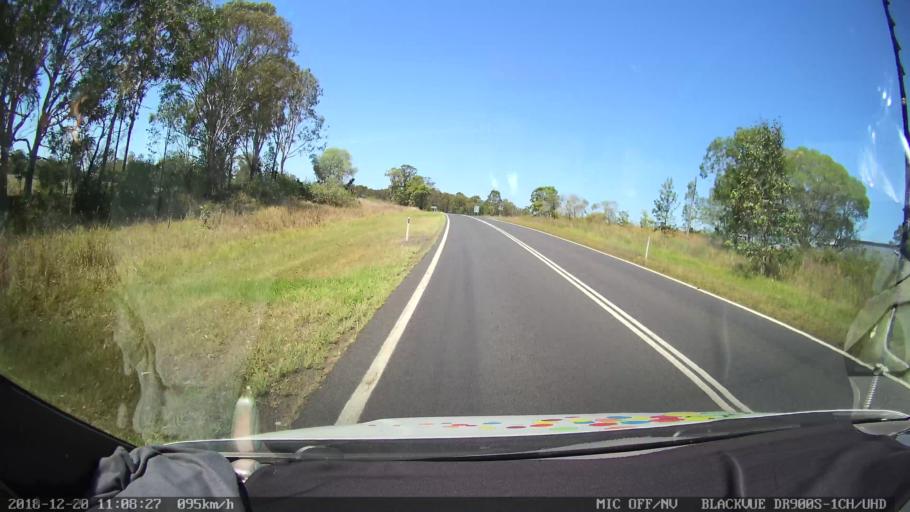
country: AU
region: New South Wales
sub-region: Richmond Valley
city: Casino
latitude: -28.9223
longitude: 153.0061
